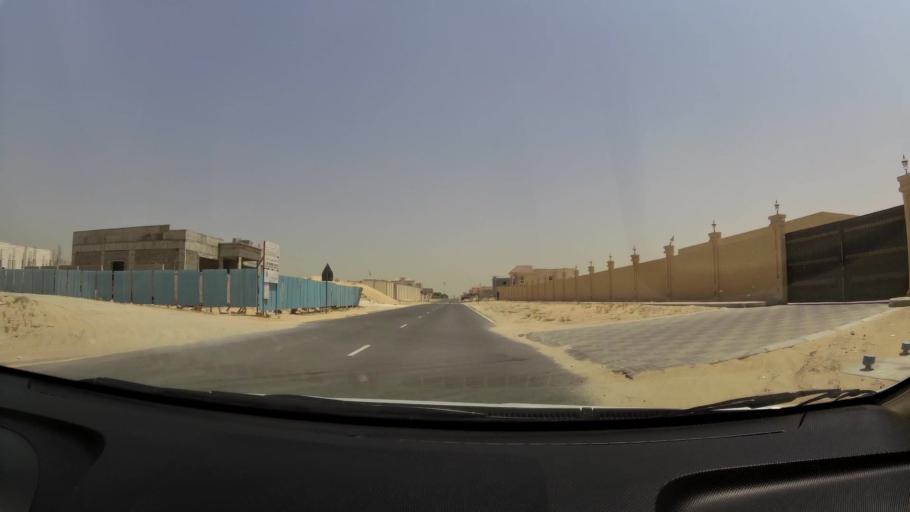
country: AE
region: Ajman
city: Ajman
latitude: 25.3993
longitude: 55.5210
